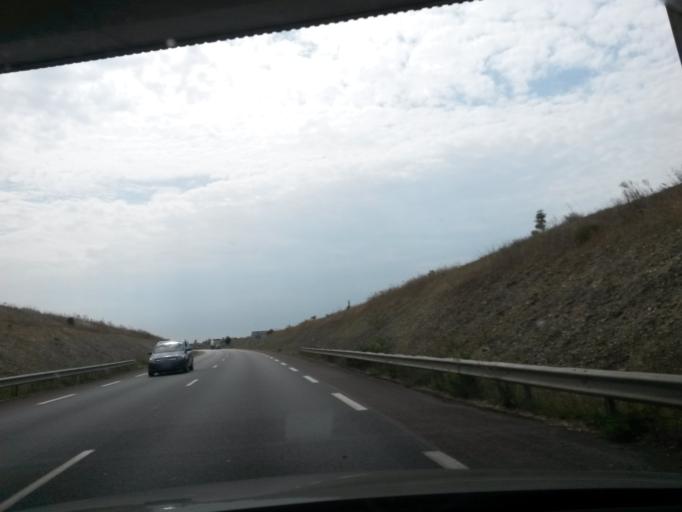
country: FR
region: Poitou-Charentes
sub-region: Departement de la Charente-Maritime
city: Saint-Xandre
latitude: 46.1851
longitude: -1.0932
